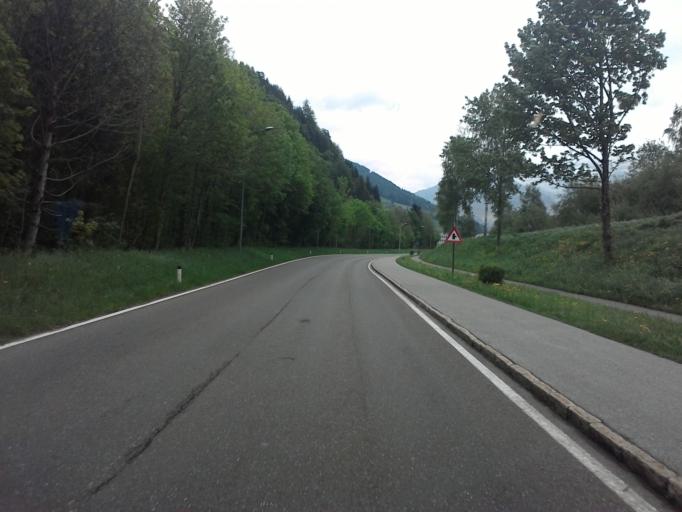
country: AT
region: Styria
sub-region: Politischer Bezirk Leoben
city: Eisenerz
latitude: 47.5643
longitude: 14.8586
